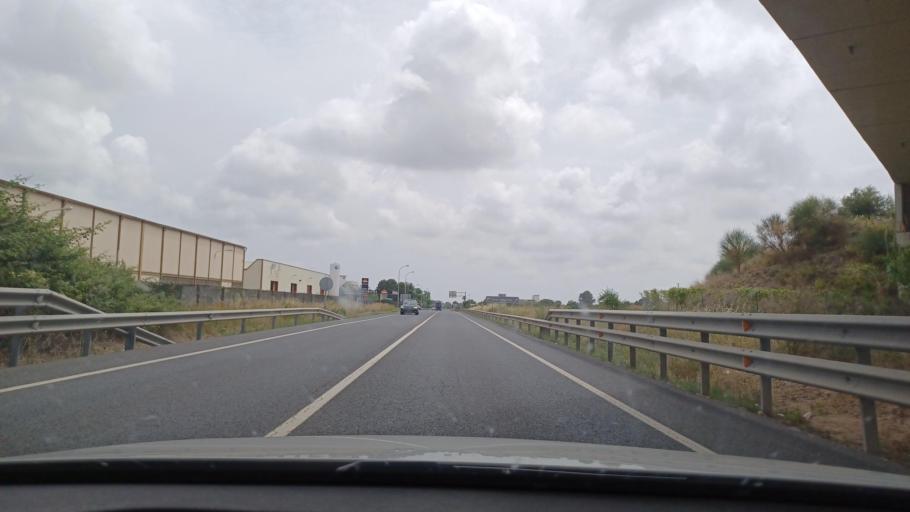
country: ES
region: Catalonia
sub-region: Provincia de Tarragona
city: la Pobla de Mafumet
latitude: 41.1913
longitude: 1.2430
